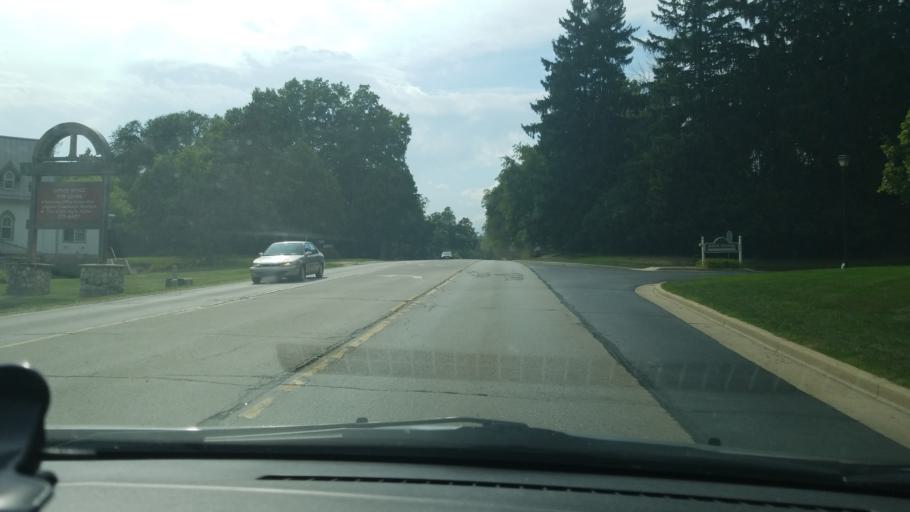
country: US
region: Wisconsin
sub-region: Ozaukee County
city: Cedarburg
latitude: 43.3019
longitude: -87.9694
